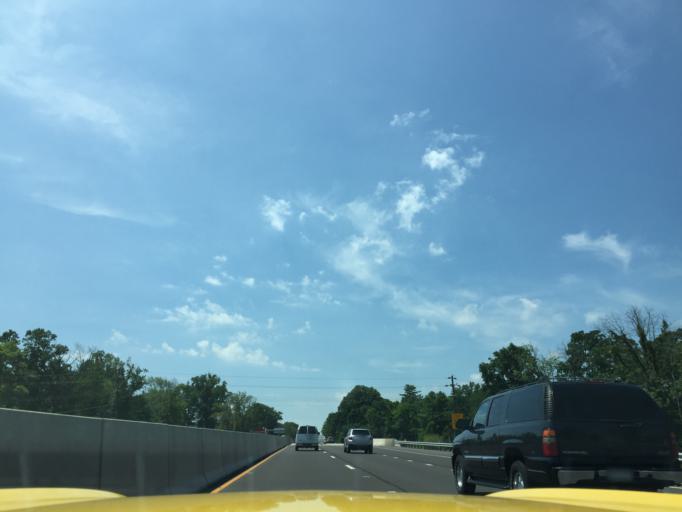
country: US
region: Pennsylvania
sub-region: Bucks County
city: Langhorne Manor
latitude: 40.1795
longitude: -74.9052
